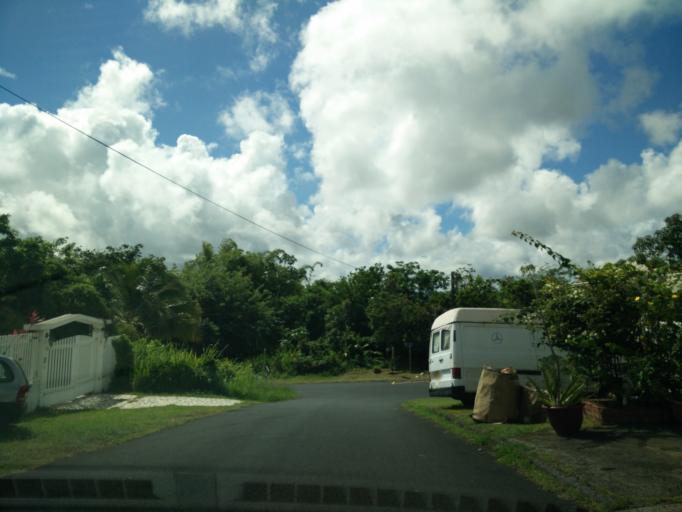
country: MQ
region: Martinique
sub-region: Martinique
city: Le Lamentin
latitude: 14.6209
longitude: -61.0173
